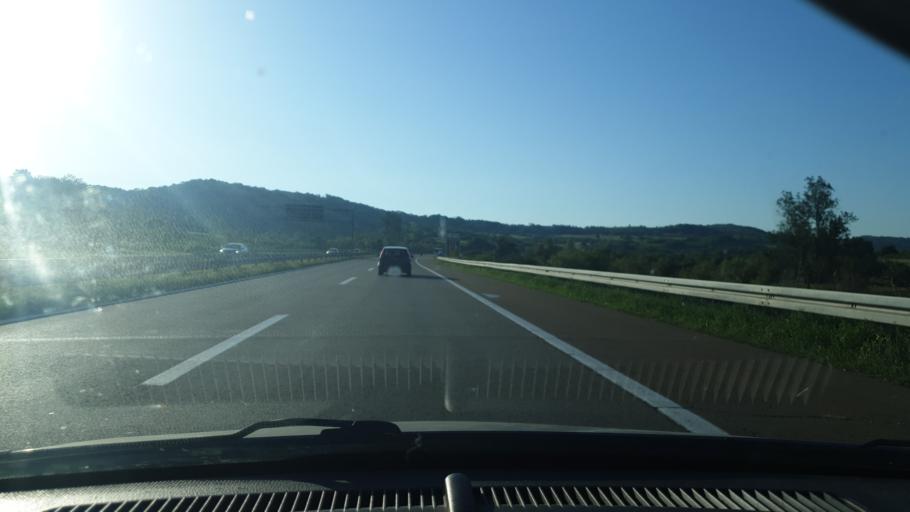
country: RS
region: Central Serbia
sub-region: Belgrade
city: Grocka
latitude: 44.6571
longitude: 20.6212
